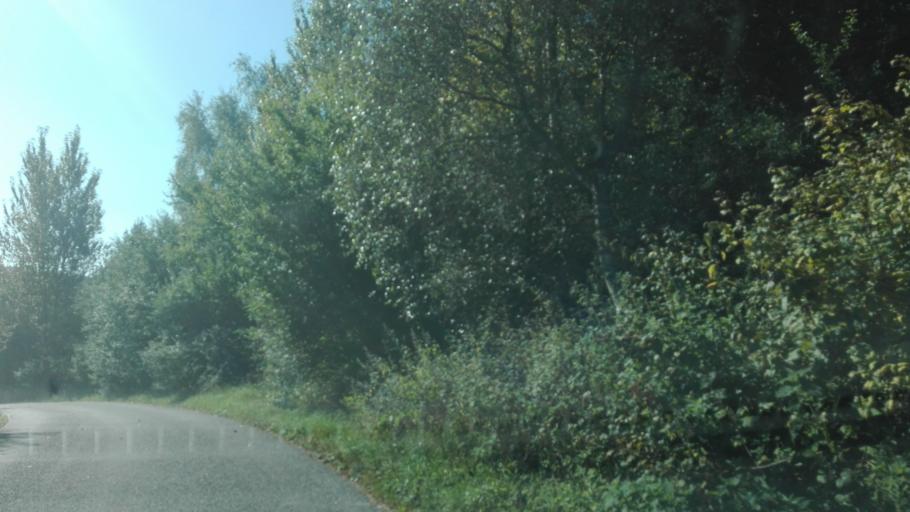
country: DK
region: Central Jutland
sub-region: Syddjurs Kommune
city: Ebeltoft
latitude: 56.2469
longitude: 10.6240
